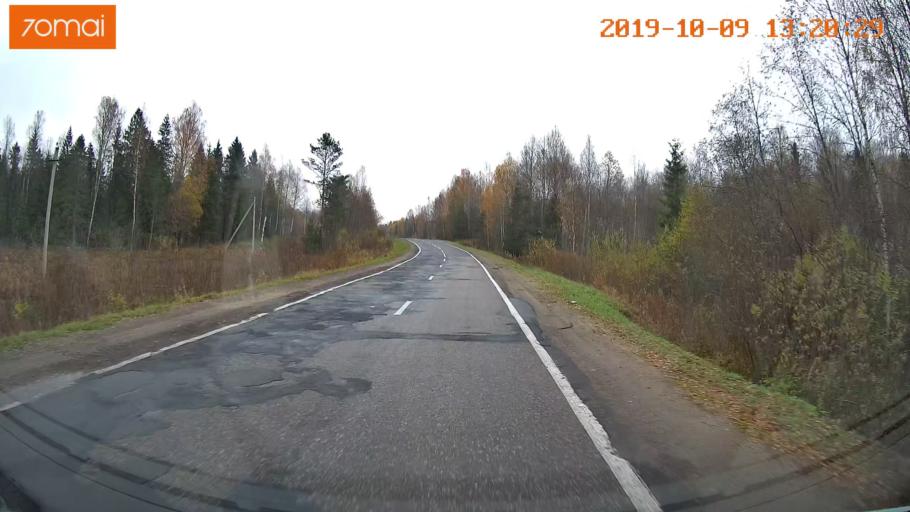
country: RU
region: Jaroslavl
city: Lyubim
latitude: 58.3427
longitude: 40.8300
